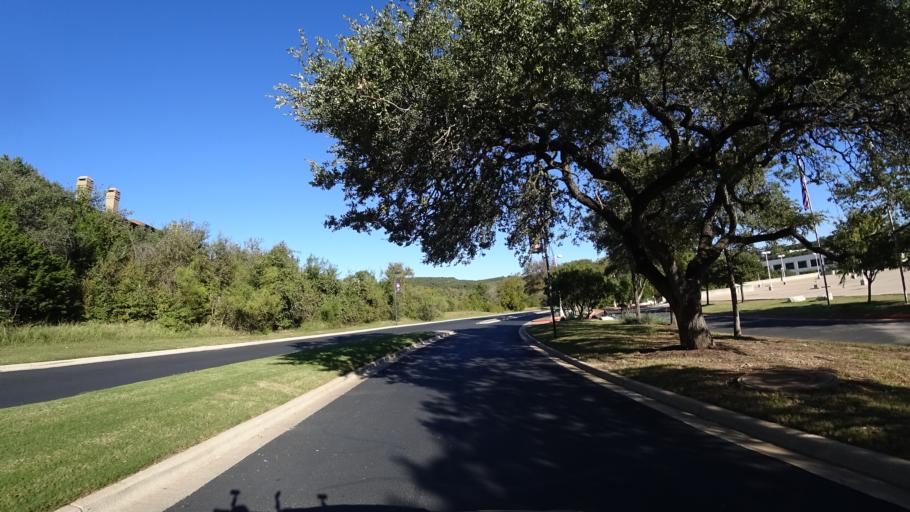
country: US
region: Texas
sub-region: Travis County
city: West Lake Hills
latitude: 30.3467
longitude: -97.8014
